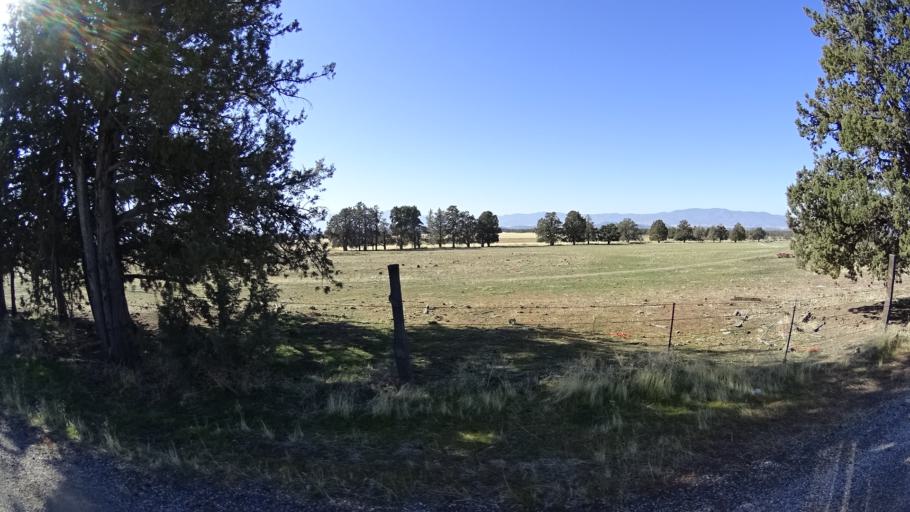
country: US
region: California
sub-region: Siskiyou County
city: Weed
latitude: 41.6254
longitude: -122.3288
